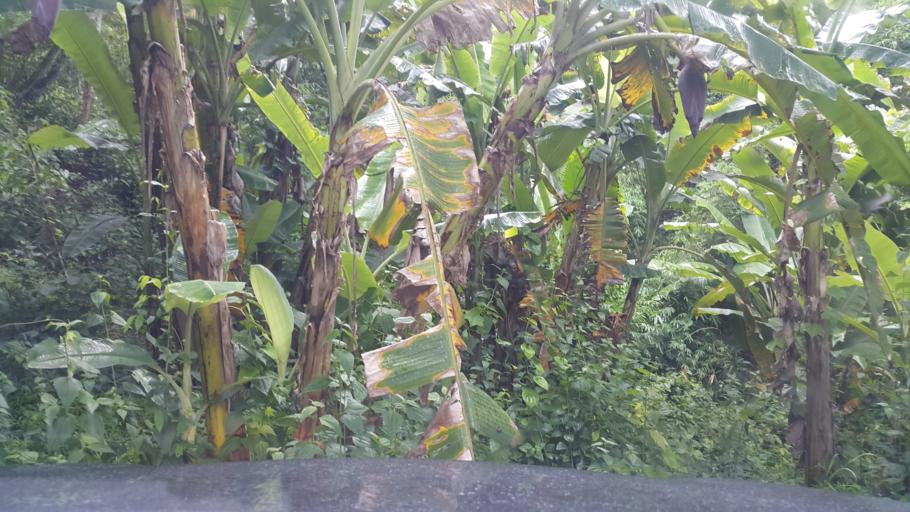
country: TH
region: Uttaradit
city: Nam Pat
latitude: 17.5146
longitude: 100.8173
